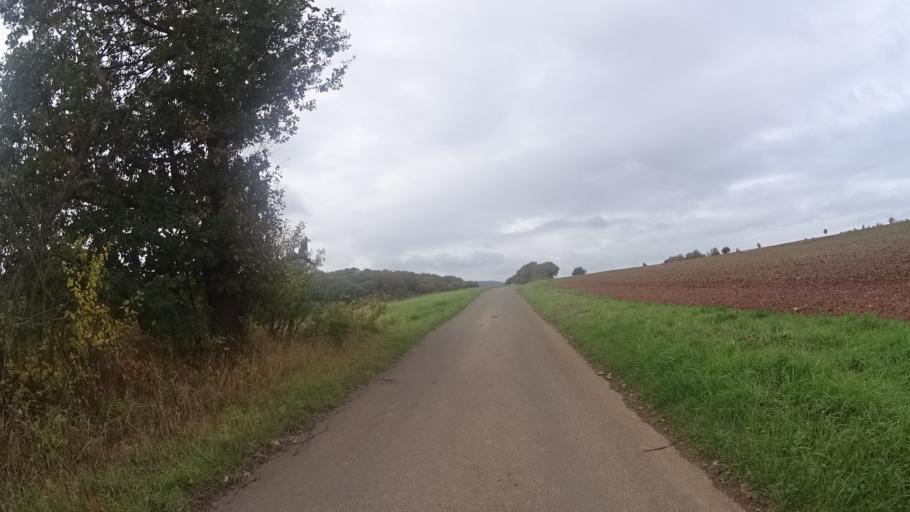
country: DE
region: Rheinland-Pfalz
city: Bolanden
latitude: 49.6435
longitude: 7.9956
